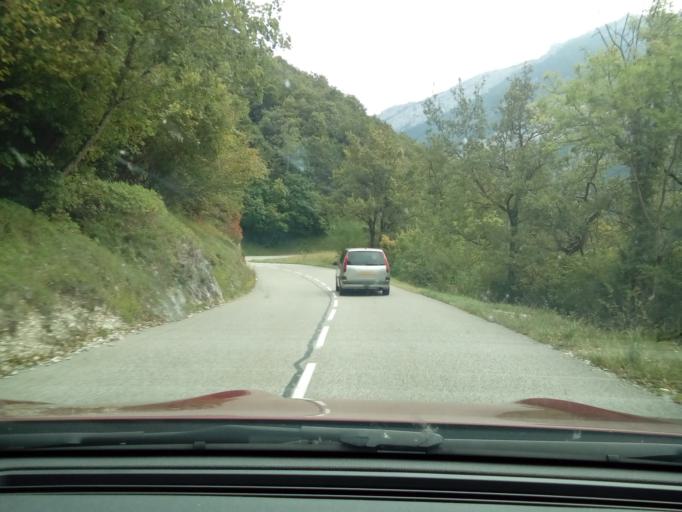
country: FR
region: Rhone-Alpes
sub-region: Departement de la Drome
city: Saint-Laurent-en-Royans
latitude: 45.0214
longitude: 5.3973
